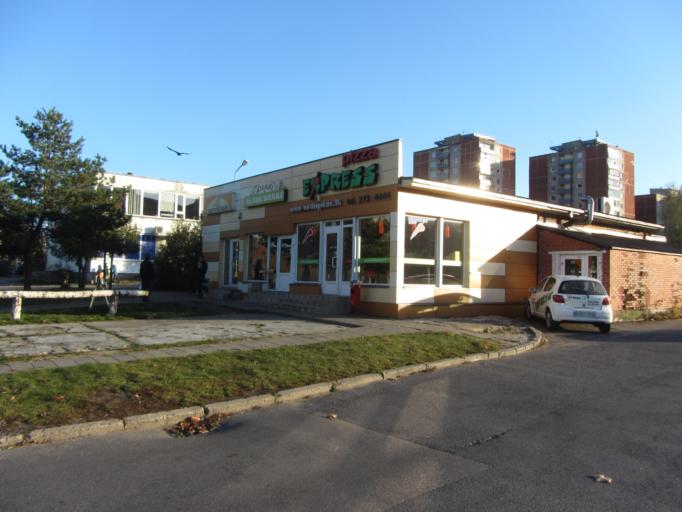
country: LT
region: Vilnius County
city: Lazdynai
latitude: 54.6857
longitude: 25.2038
